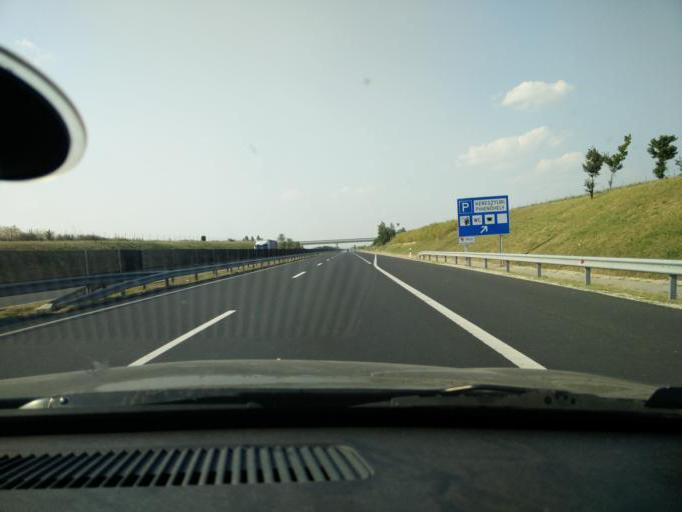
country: HU
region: Fejer
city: Rackeresztur
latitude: 47.2790
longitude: 18.8617
